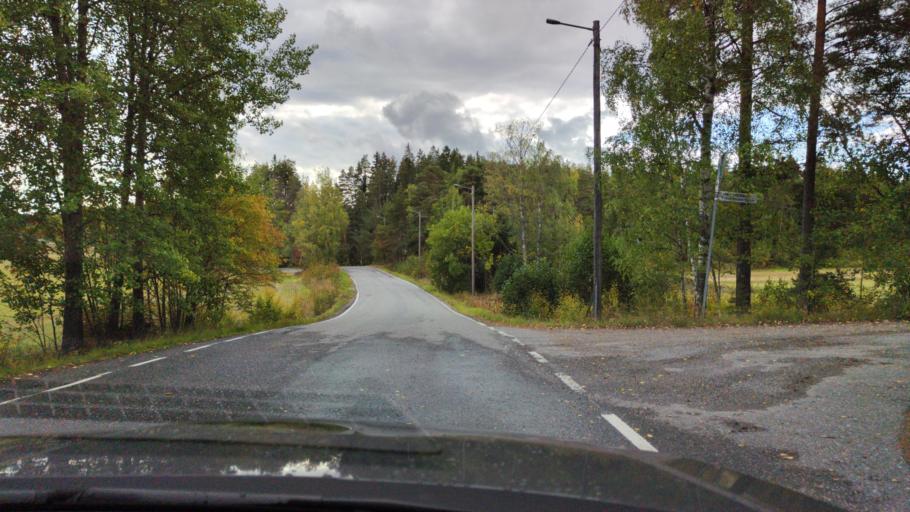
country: FI
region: Varsinais-Suomi
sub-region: Aboland-Turunmaa
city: Pargas
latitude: 60.3697
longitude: 22.2763
